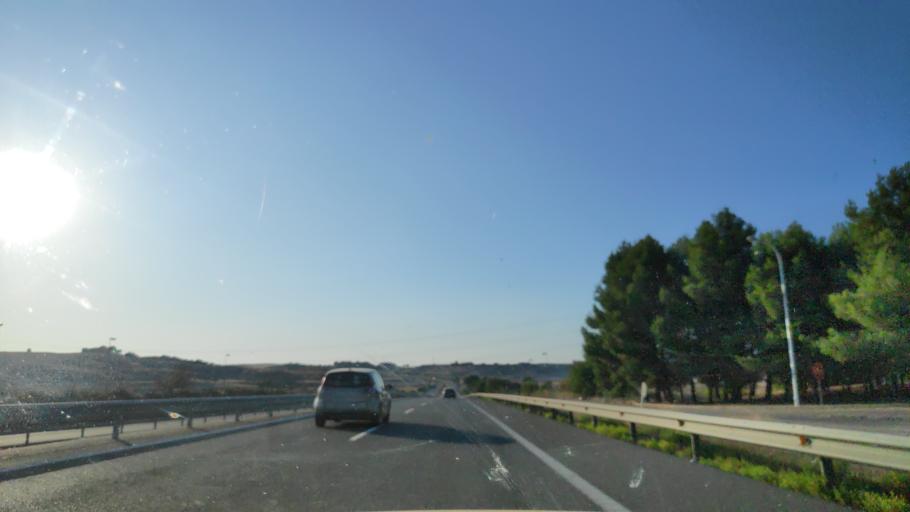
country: ES
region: Castille-La Mancha
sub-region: Provincia de Cuenca
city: Belinchon
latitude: 40.0329
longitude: -3.0420
